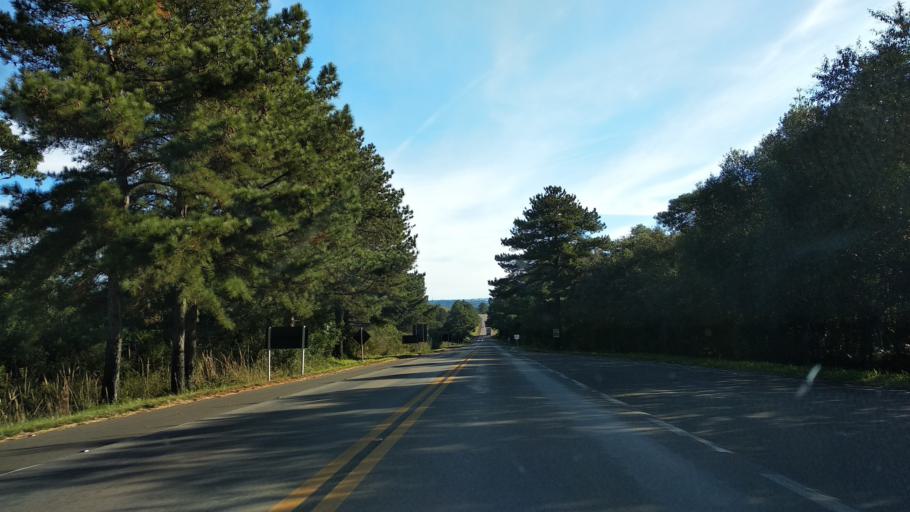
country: BR
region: Santa Catarina
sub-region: Celso Ramos
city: Celso Ramos
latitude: -27.5303
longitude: -51.3893
